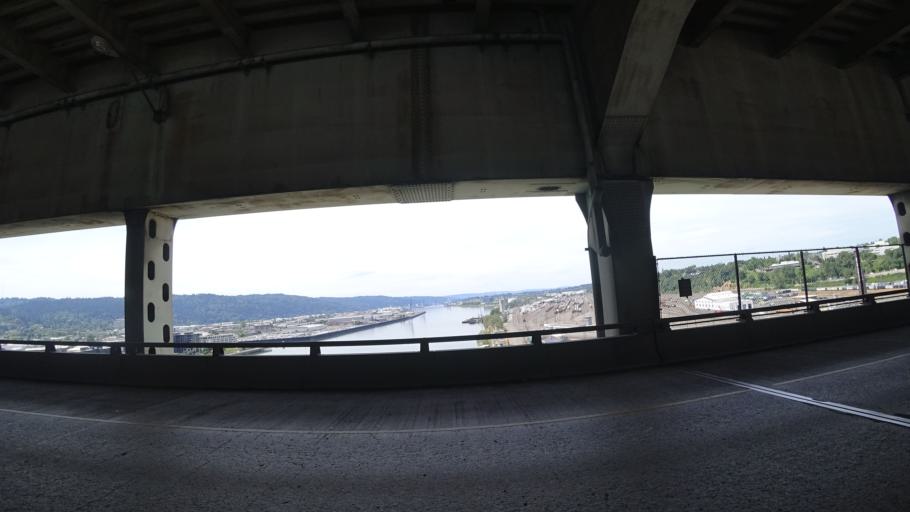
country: US
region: Oregon
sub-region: Multnomah County
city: Portland
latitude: 45.5437
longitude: -122.6808
